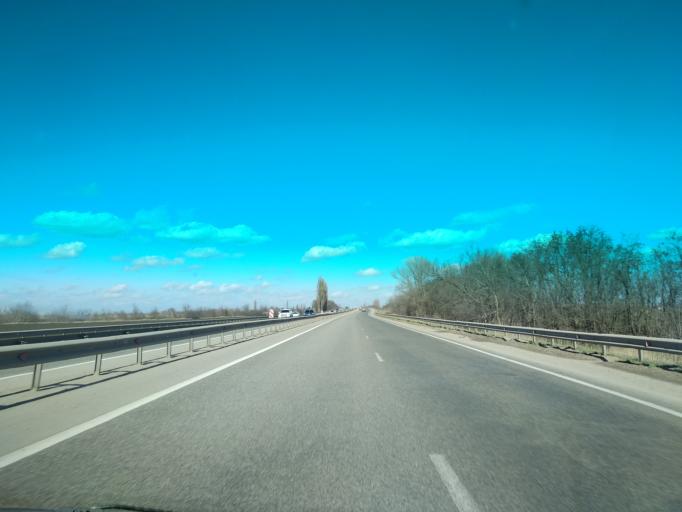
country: RU
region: Krasnodarskiy
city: Agronom
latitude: 45.1450
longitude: 39.1095
